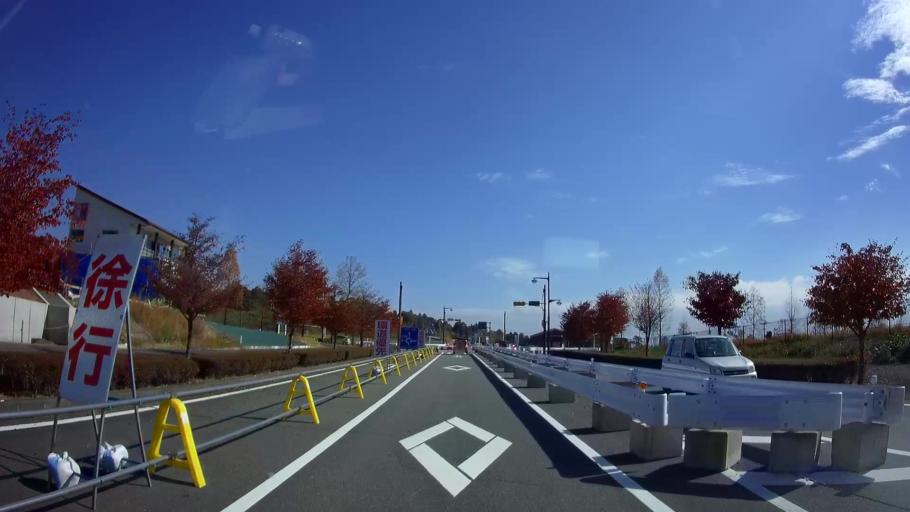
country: JP
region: Gunma
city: Annaka
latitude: 36.3608
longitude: 138.8483
